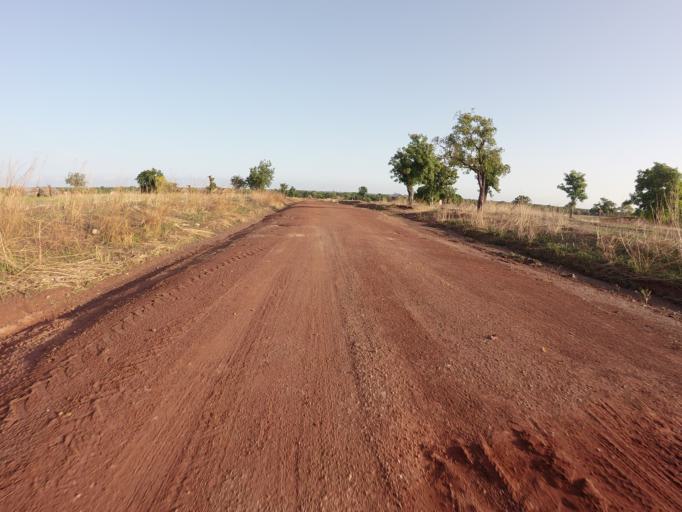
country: TG
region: Savanes
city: Sansanne-Mango
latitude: 10.3536
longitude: -0.0931
